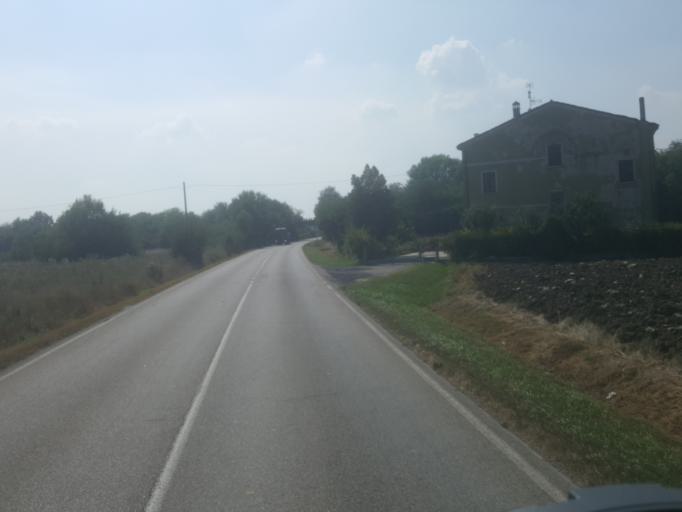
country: IT
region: Lombardy
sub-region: Provincia di Cremona
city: Casalmaggiore
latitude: 44.9630
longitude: 10.3966
